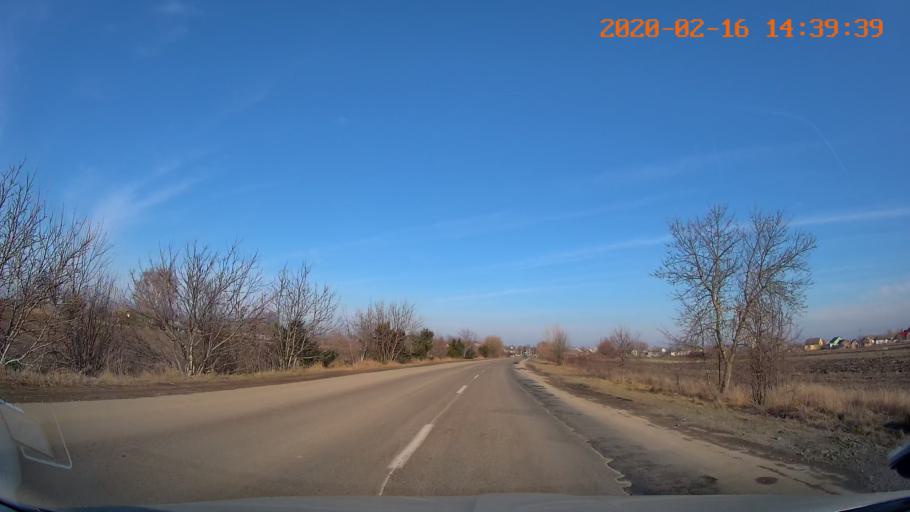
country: RO
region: Botosani
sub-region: Comuna Darabani
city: Bajura
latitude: 48.2453
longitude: 26.5513
